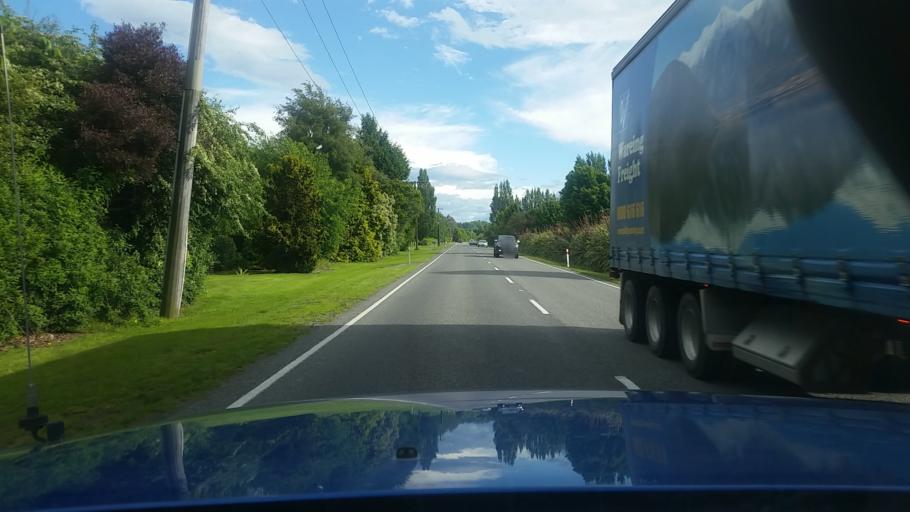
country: NZ
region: Canterbury
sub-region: Ashburton District
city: Ashburton
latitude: -43.8718
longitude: 171.7275
